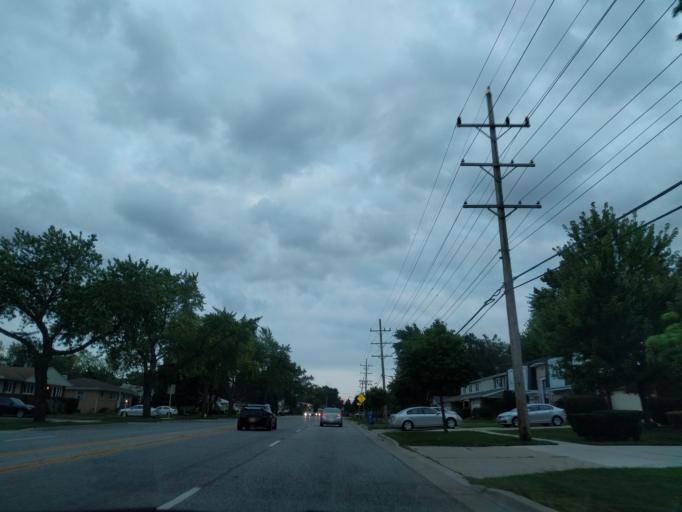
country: US
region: Illinois
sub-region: Cook County
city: Mount Prospect
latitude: 42.0462
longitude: -87.9602
